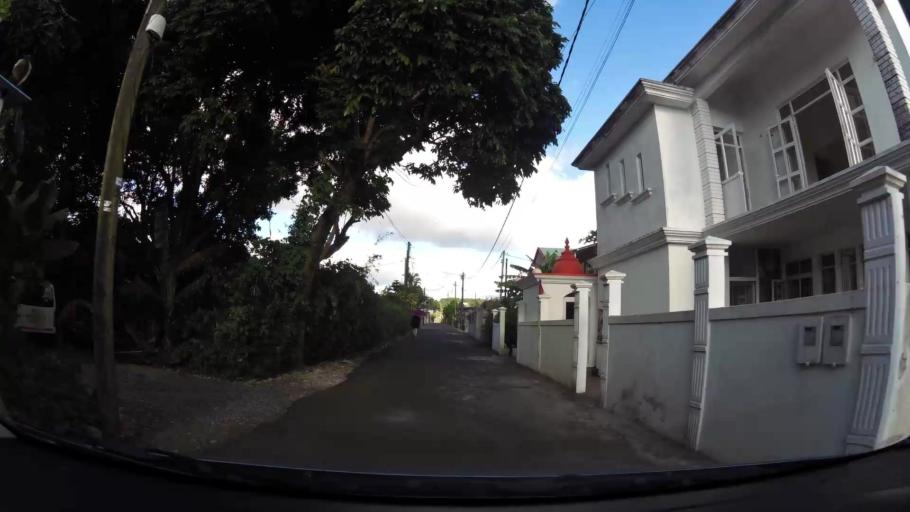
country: MU
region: Plaines Wilhems
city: Curepipe
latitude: -20.2901
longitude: 57.5190
